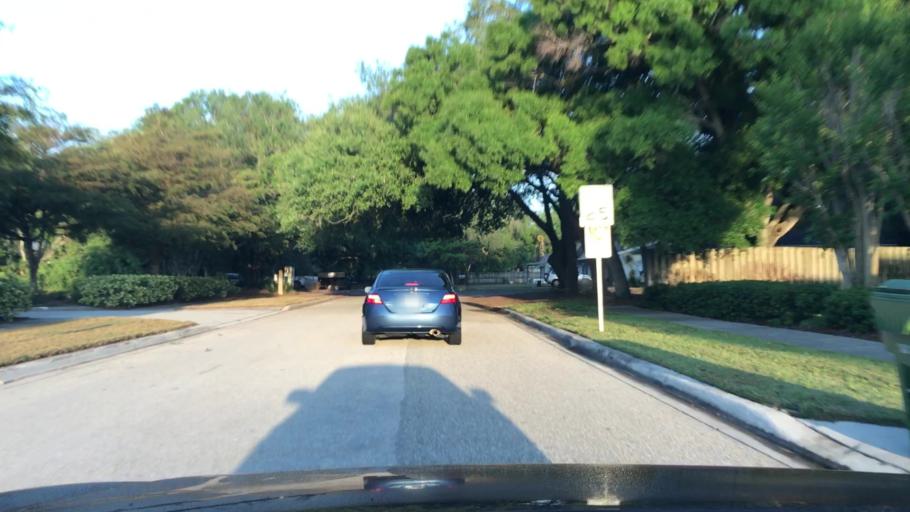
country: US
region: Florida
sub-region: Sarasota County
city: Sarasota
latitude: 27.3356
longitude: -82.5145
